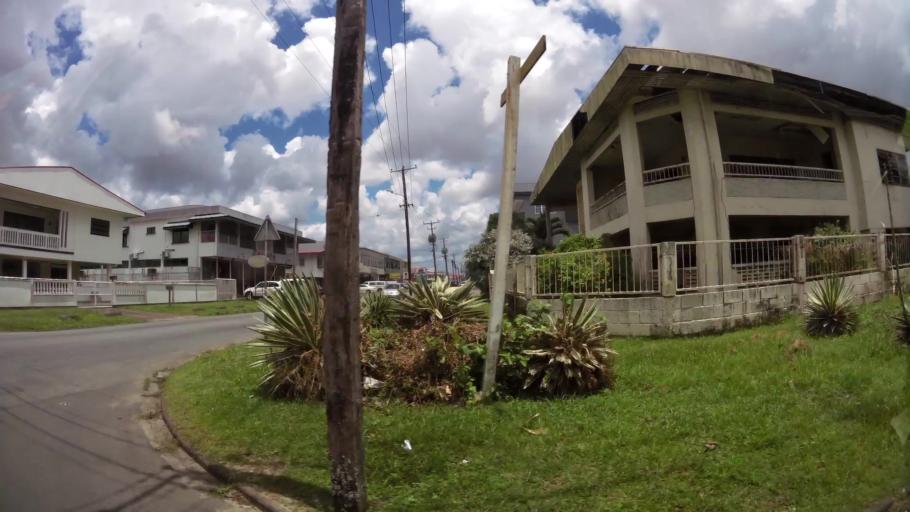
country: SR
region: Paramaribo
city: Paramaribo
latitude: 5.8513
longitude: -55.1386
